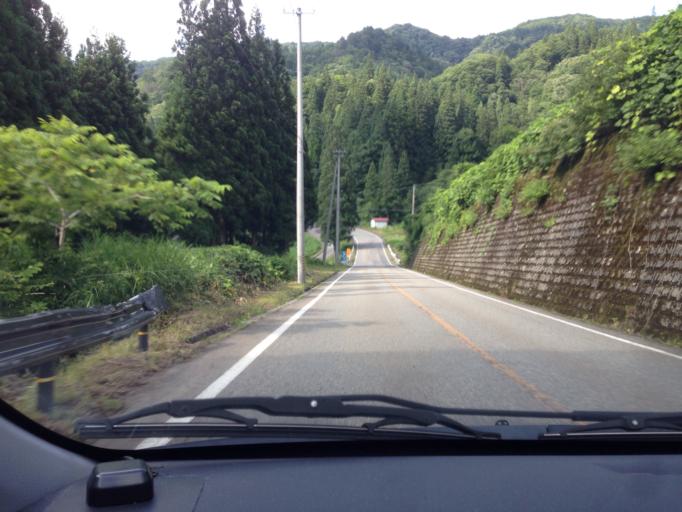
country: JP
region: Fukushima
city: Kitakata
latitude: 37.4265
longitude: 139.5388
